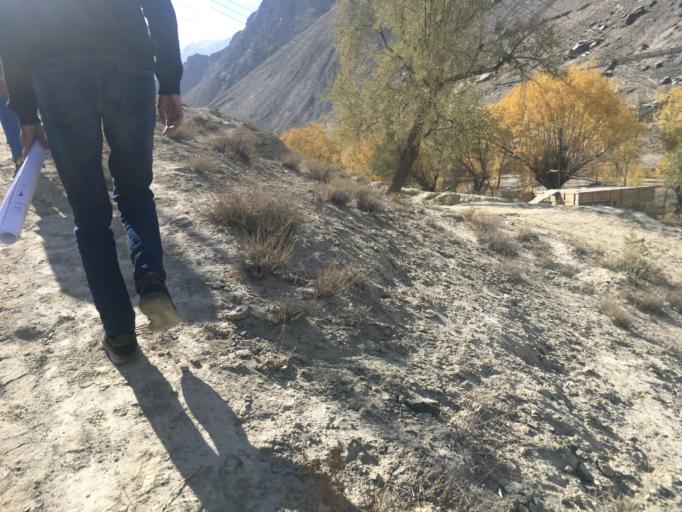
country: PK
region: Gilgit-Baltistan
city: Skardu
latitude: 35.3314
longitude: 75.5218
